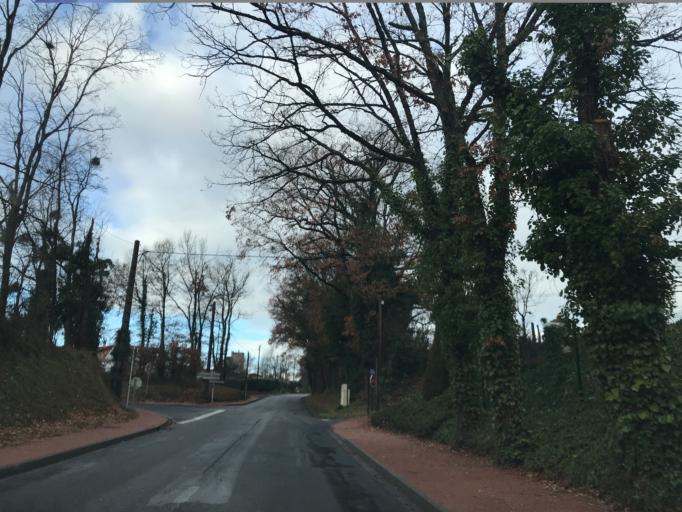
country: FR
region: Auvergne
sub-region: Departement du Puy-de-Dome
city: Peschadoires
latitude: 45.8558
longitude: 3.5249
